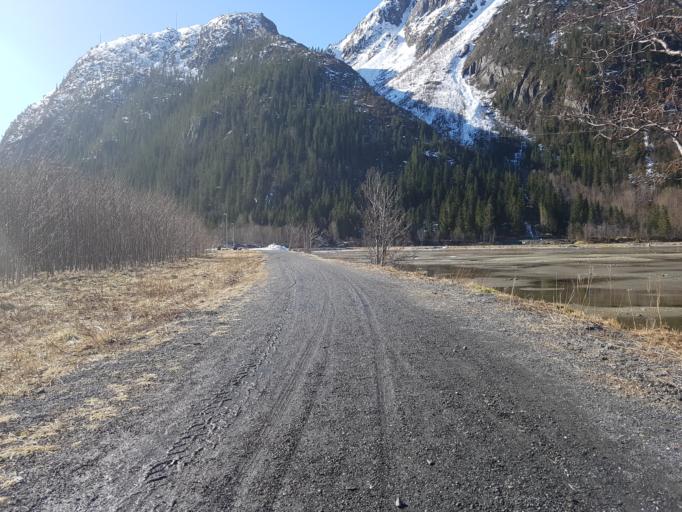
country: NO
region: Nordland
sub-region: Vefsn
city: Mosjoen
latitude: 65.8316
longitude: 13.1932
